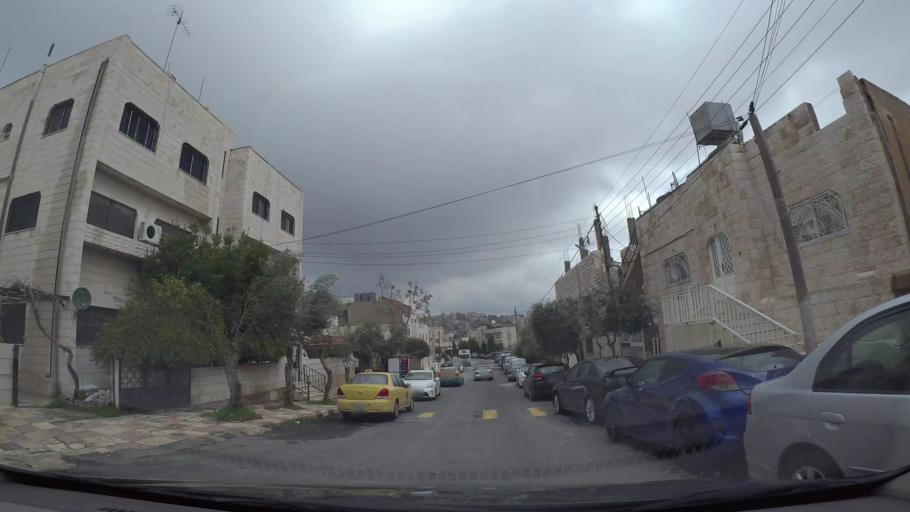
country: JO
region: Amman
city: Amman
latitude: 31.9409
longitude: 35.9033
